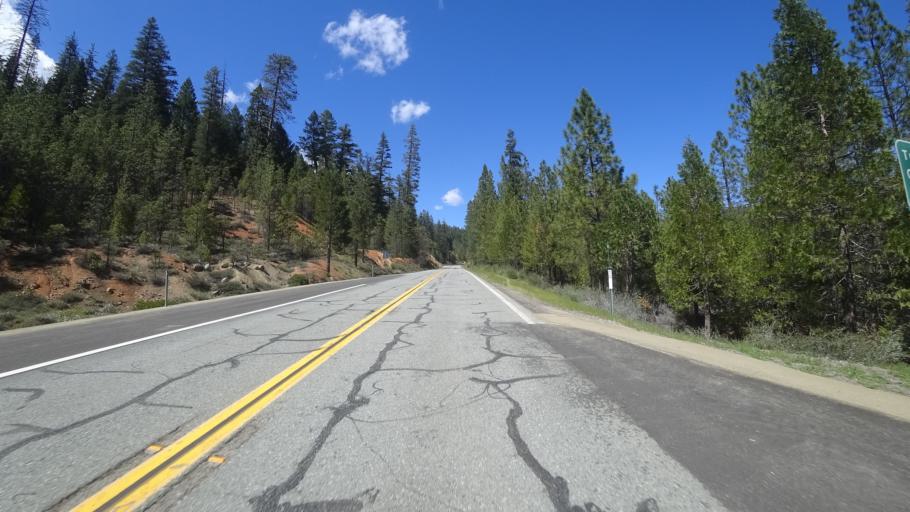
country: US
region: California
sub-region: Trinity County
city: Lewiston
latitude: 40.8720
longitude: -122.8027
